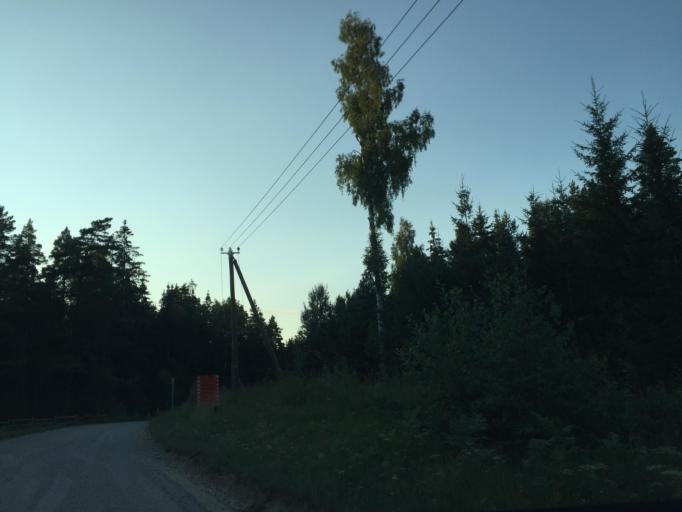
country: LV
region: Kuldigas Rajons
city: Kuldiga
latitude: 57.1139
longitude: 22.2145
